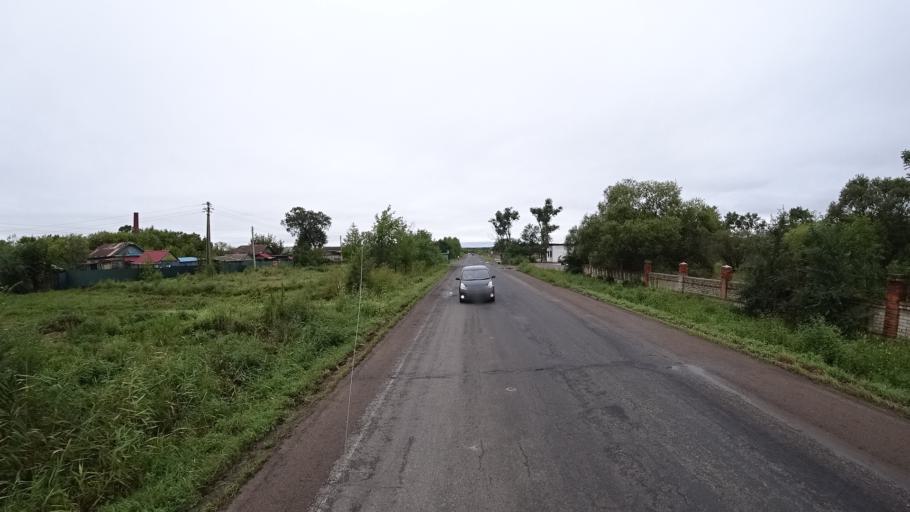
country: RU
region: Primorskiy
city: Monastyrishche
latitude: 44.2012
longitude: 132.4759
